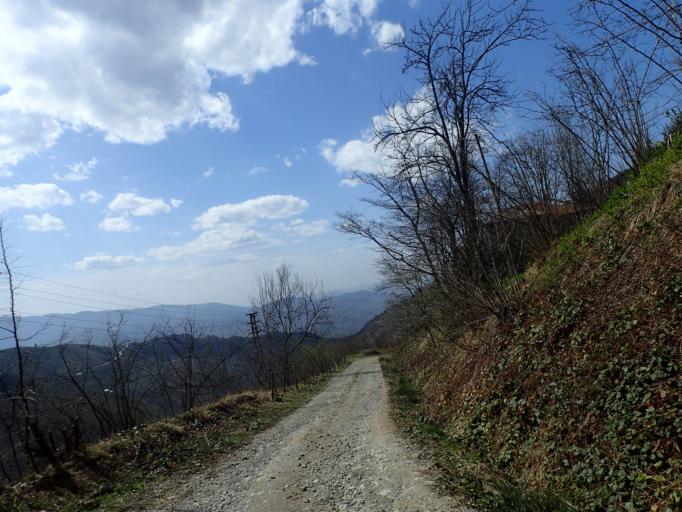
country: TR
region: Ordu
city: Kabaduz
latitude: 40.8168
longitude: 37.9053
